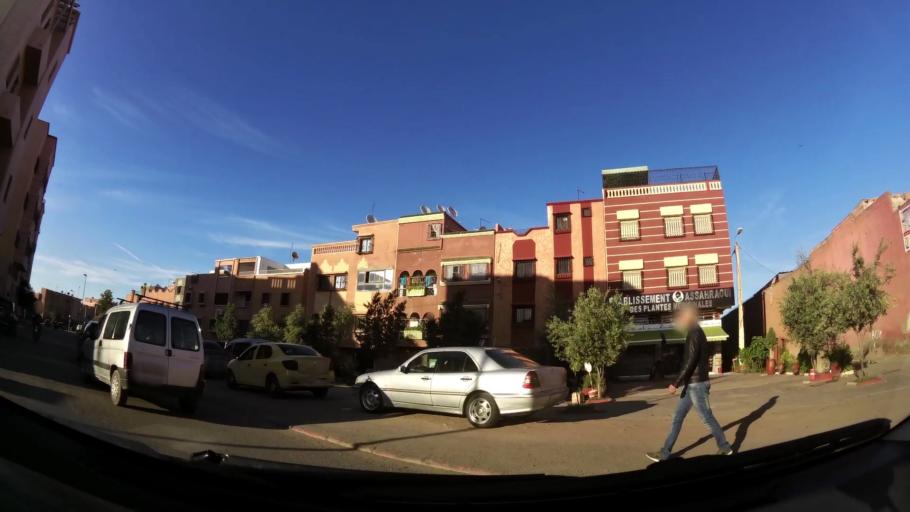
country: MA
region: Marrakech-Tensift-Al Haouz
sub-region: Marrakech
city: Marrakesh
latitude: 31.6192
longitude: -8.0583
